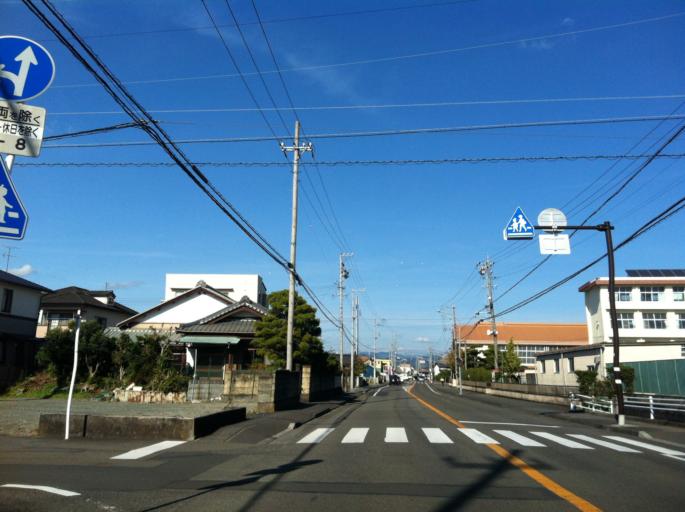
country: JP
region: Shizuoka
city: Fujieda
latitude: 34.8421
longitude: 138.2690
